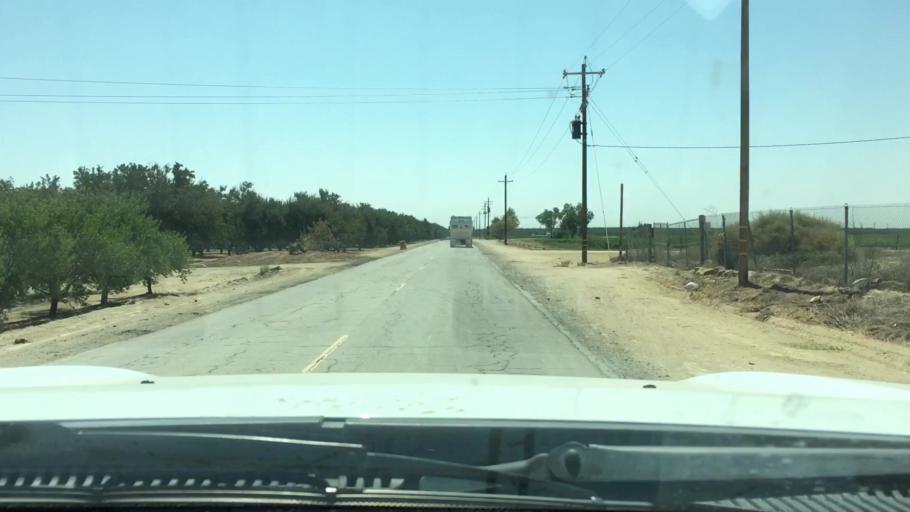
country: US
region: California
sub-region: Kern County
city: Wasco
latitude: 35.5080
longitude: -119.4034
